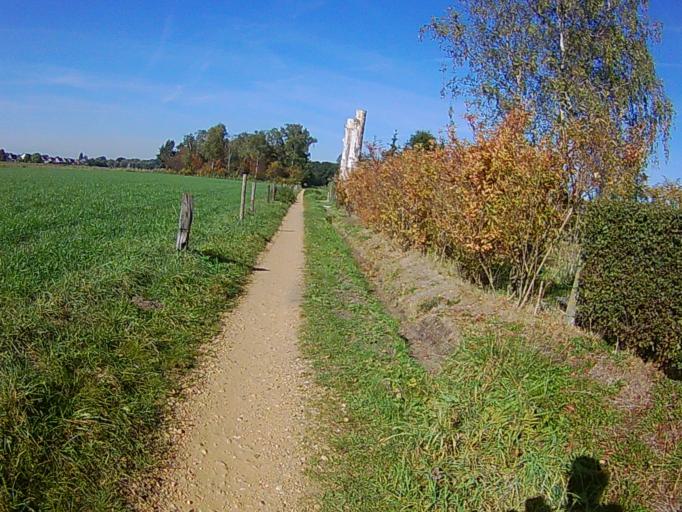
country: BE
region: Flanders
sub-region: Provincie Antwerpen
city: Stabroek
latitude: 51.3316
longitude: 4.3908
